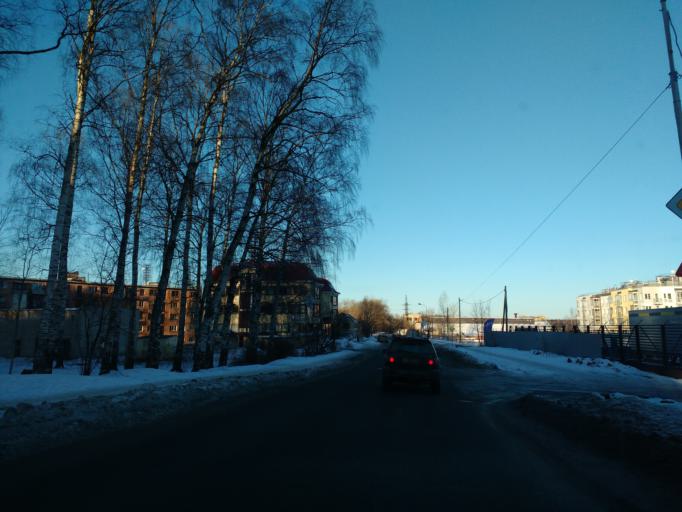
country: RU
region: Republic of Karelia
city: Petrozavodsk
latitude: 61.7812
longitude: 34.3734
